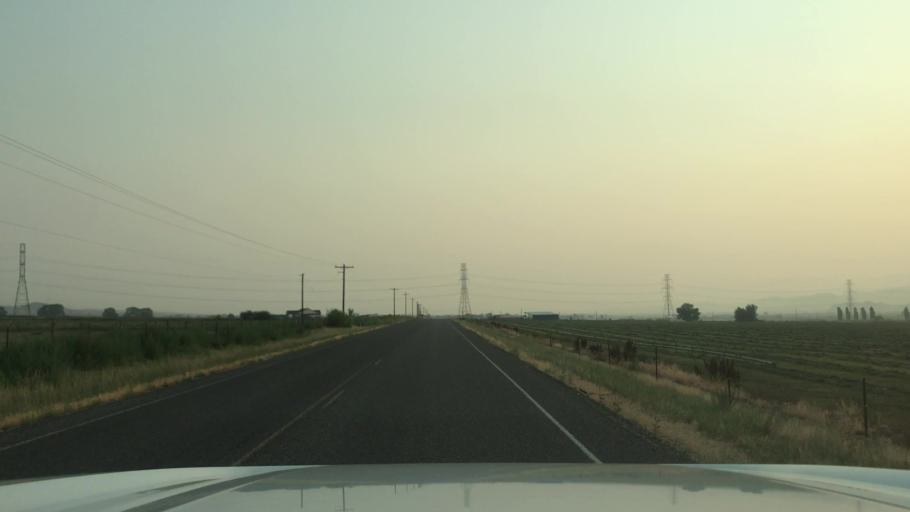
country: US
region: Utah
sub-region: Sevier County
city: Aurora
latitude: 38.8930
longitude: -111.9526
